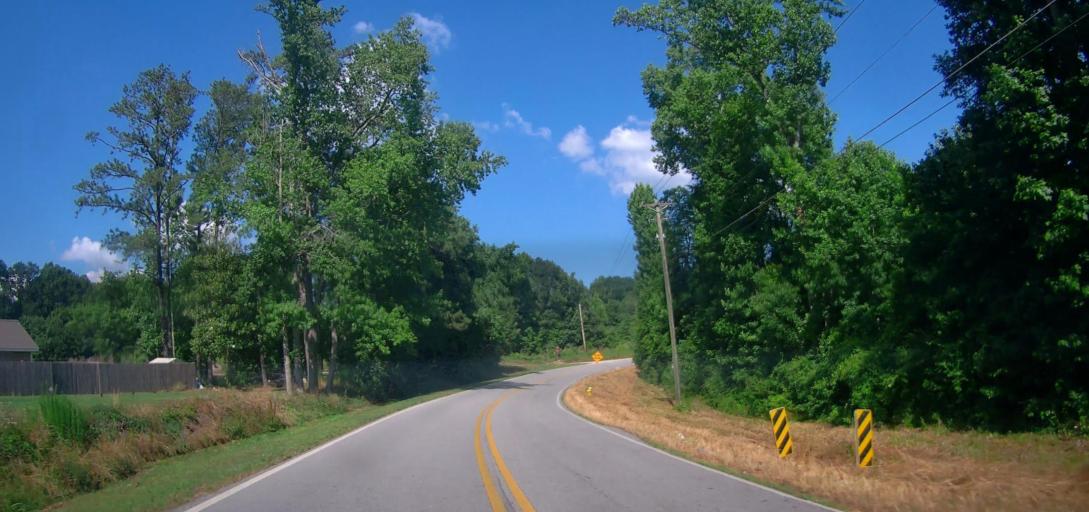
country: US
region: Georgia
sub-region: Spalding County
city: East Griffin
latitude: 33.2912
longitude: -84.2095
